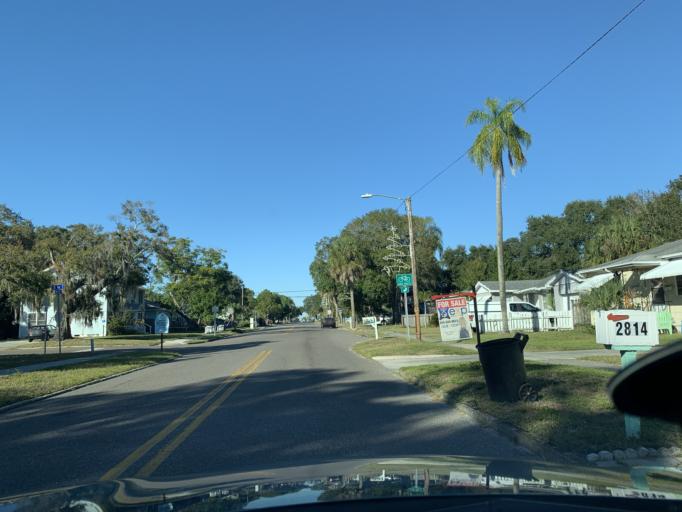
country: US
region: Florida
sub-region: Pinellas County
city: Gulfport
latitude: 27.7419
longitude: -82.6997
